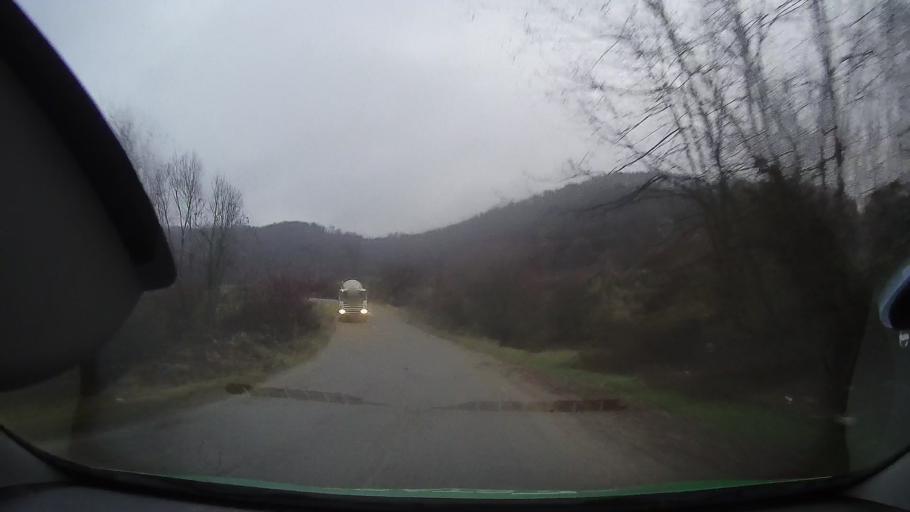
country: RO
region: Hunedoara
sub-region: Comuna Ribita
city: Ribita
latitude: 46.2341
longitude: 22.7459
